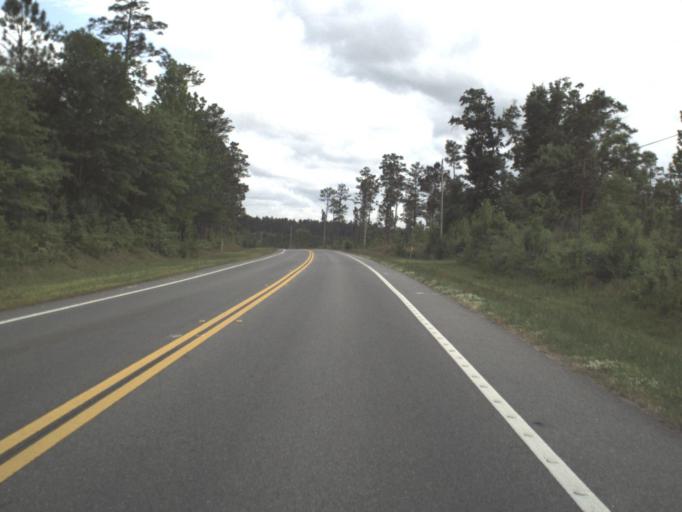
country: US
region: Alabama
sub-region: Escambia County
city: East Brewton
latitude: 30.9640
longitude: -87.0468
